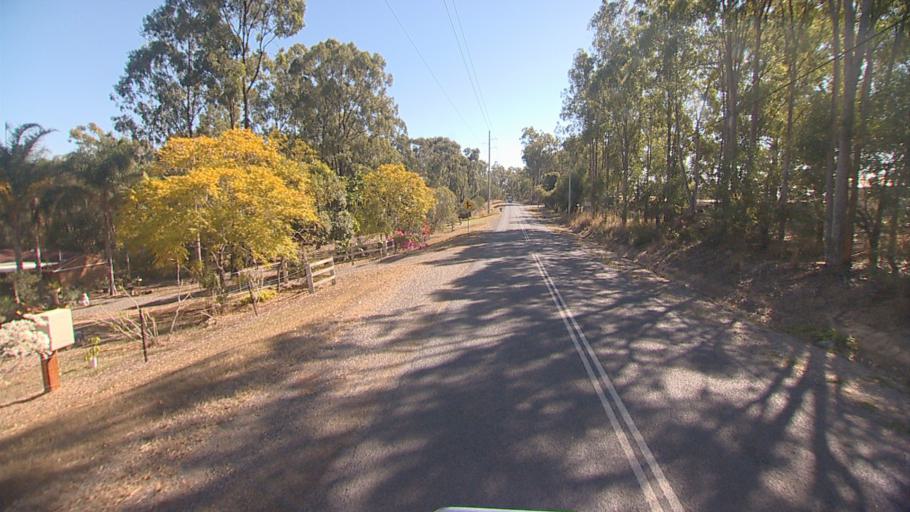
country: AU
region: Queensland
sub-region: Logan
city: Cedar Vale
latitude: -27.8837
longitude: 153.0168
